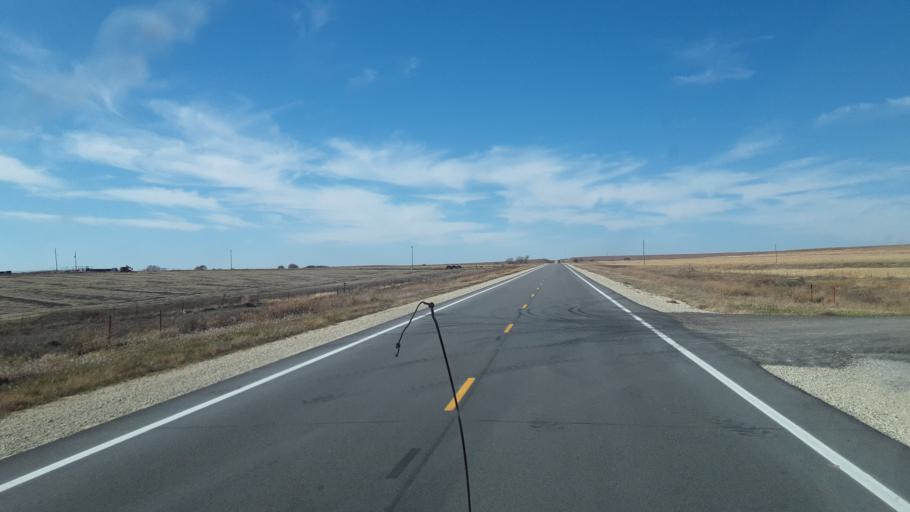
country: US
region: Kansas
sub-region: Chase County
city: Cottonwood Falls
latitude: 38.3628
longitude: -96.6681
